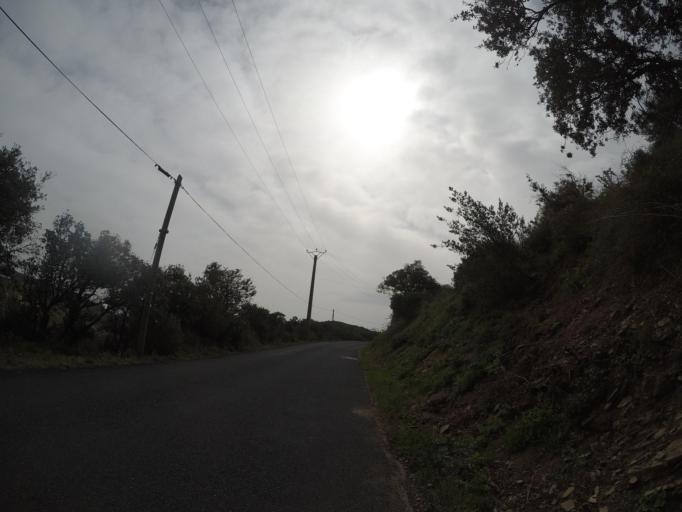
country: FR
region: Languedoc-Roussillon
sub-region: Departement des Pyrenees-Orientales
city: Corneilla-la-Riviere
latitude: 42.7303
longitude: 2.7385
